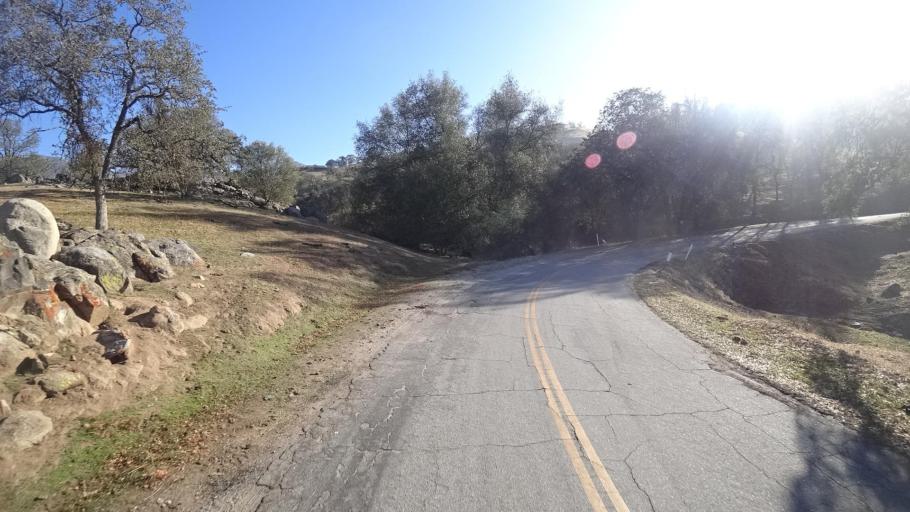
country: US
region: California
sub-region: Kern County
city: Alta Sierra
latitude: 35.7302
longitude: -118.8104
